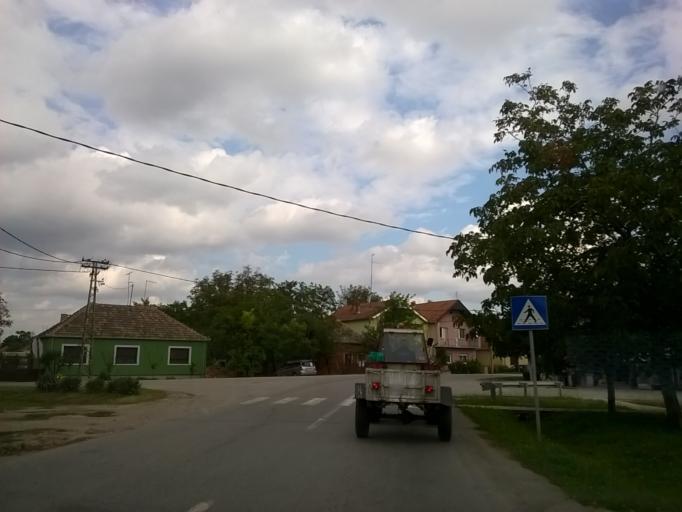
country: RS
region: Autonomna Pokrajina Vojvodina
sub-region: Juznobanatski Okrug
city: Plandiste
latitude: 45.2288
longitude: 21.1307
